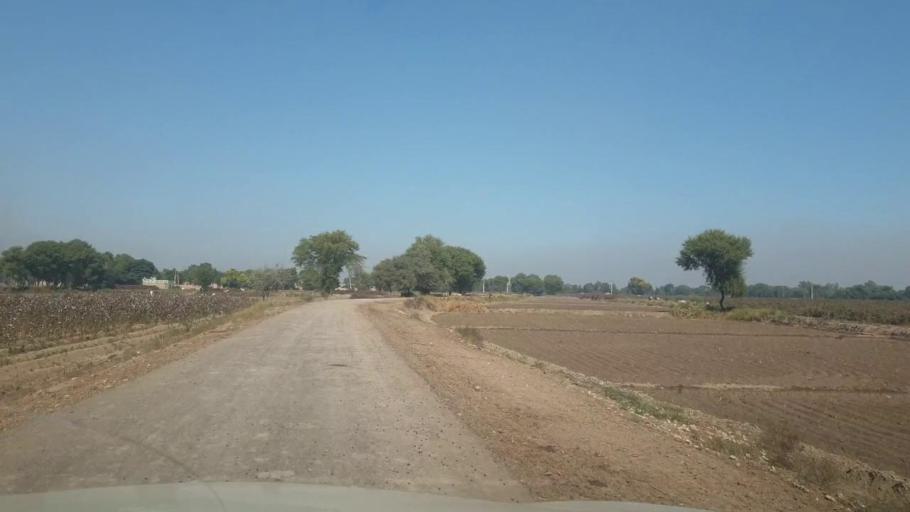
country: PK
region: Sindh
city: Bhan
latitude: 26.5810
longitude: 67.7000
